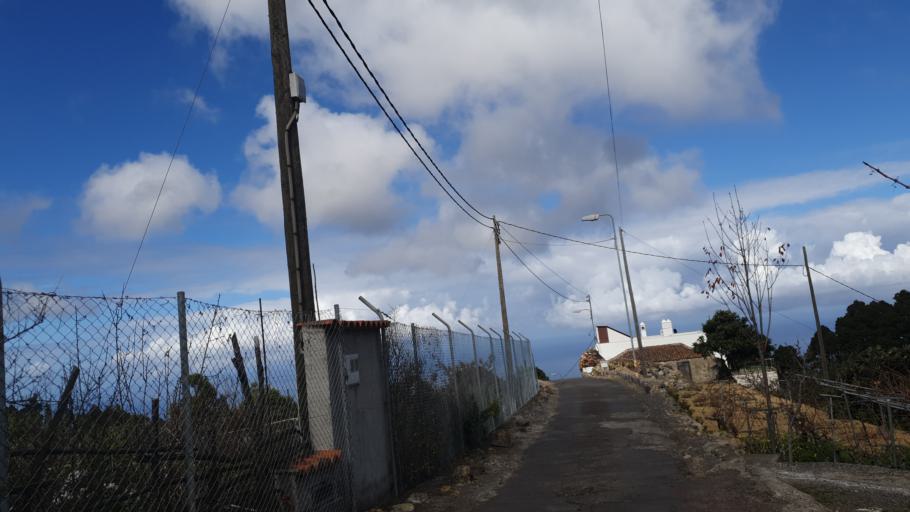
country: ES
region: Canary Islands
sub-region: Provincia de Santa Cruz de Tenerife
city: Icod de los Vinos
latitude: 28.3535
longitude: -16.6862
